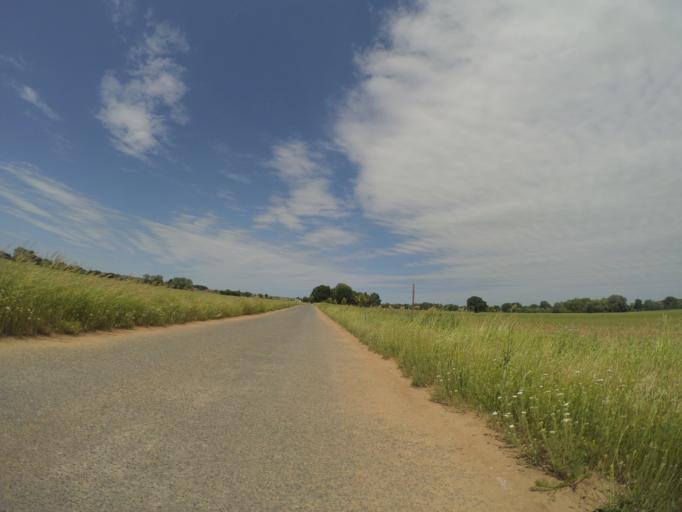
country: CZ
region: Central Bohemia
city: Milovice
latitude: 50.1736
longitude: 14.8858
